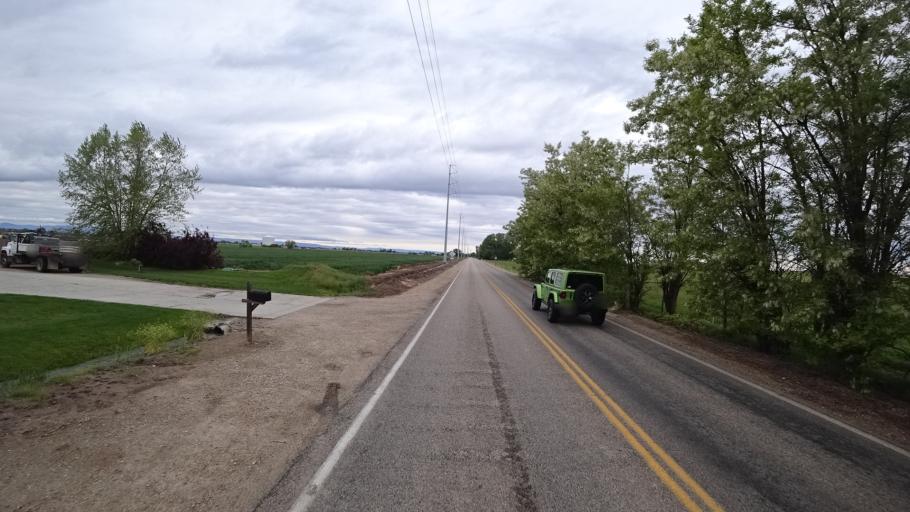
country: US
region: Idaho
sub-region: Ada County
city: Star
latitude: 43.6486
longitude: -116.4945
